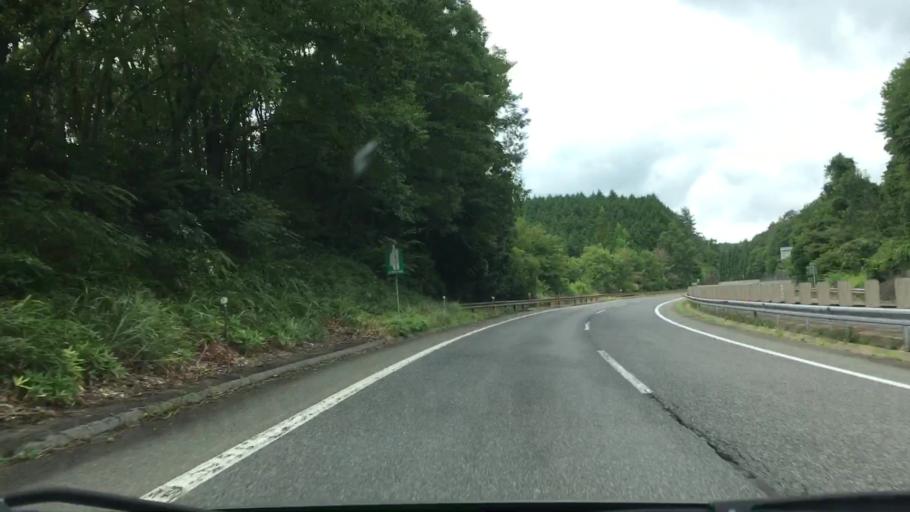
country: JP
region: Hiroshima
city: Shobara
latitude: 34.8927
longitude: 133.2149
